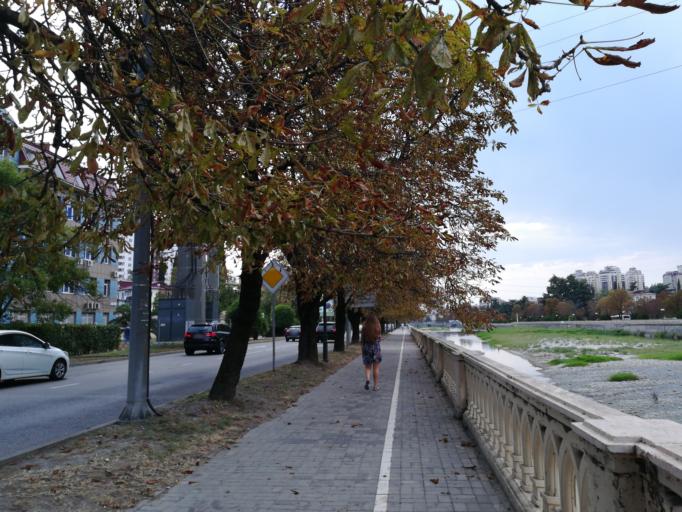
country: RU
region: Krasnodarskiy
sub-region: Sochi City
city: Sochi
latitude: 43.5995
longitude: 39.7293
